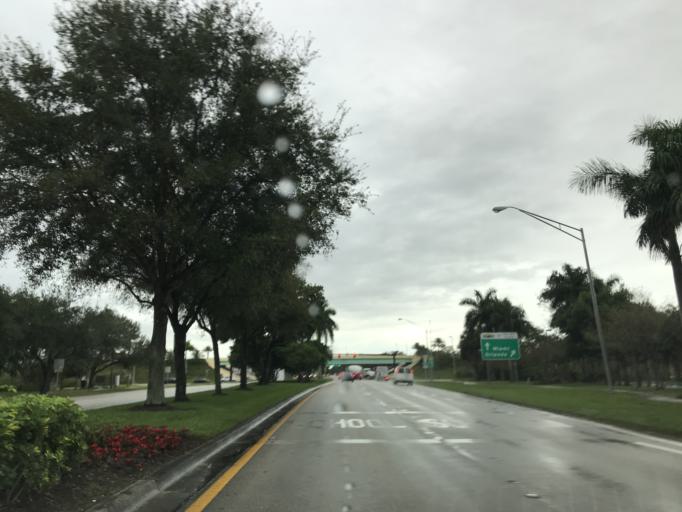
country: US
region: Florida
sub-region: Broward County
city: Coral Springs
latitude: 26.3002
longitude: -80.2788
